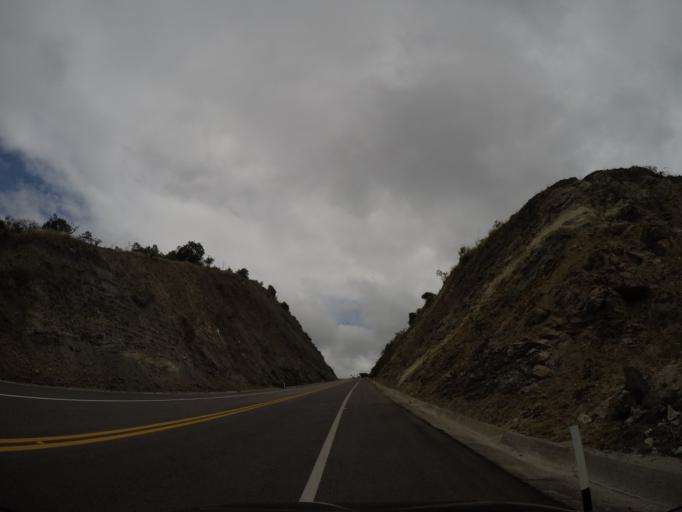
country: MX
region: Oaxaca
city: San Lorenzo Albarradas
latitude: 16.9327
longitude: -96.2669
